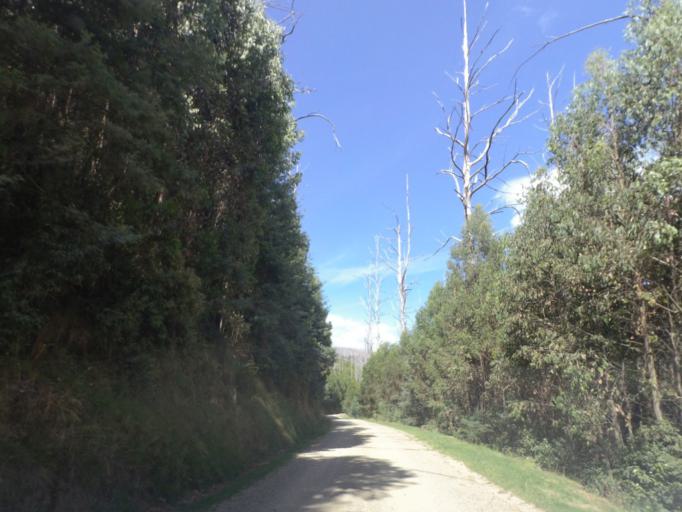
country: AU
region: Victoria
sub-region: Murrindindi
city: Alexandra
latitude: -37.4485
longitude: 145.7839
